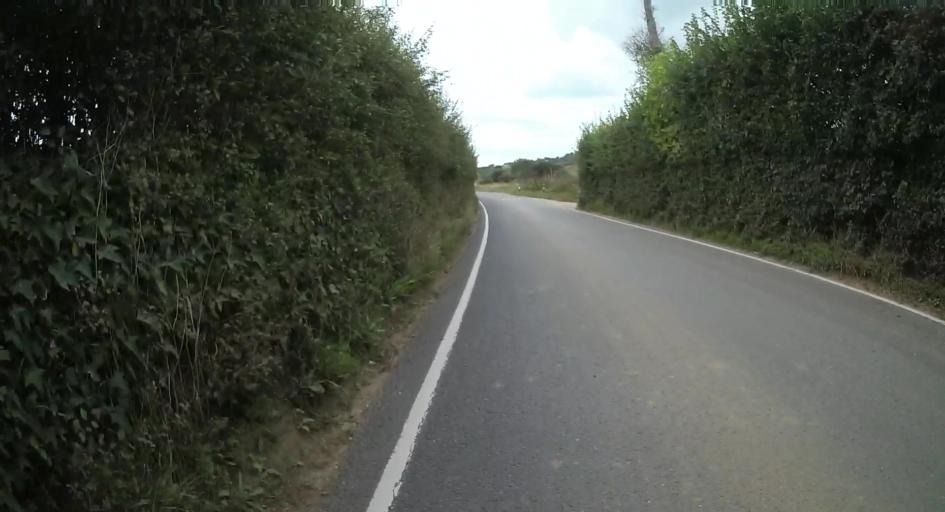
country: GB
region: England
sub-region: Isle of Wight
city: Niton
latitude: 50.6096
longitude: -1.2692
